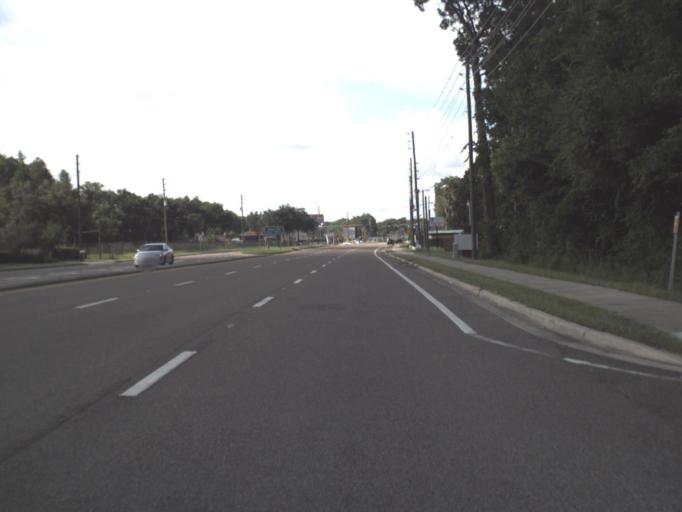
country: US
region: Florida
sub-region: Pasco County
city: Land O' Lakes
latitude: 28.2297
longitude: -82.4583
